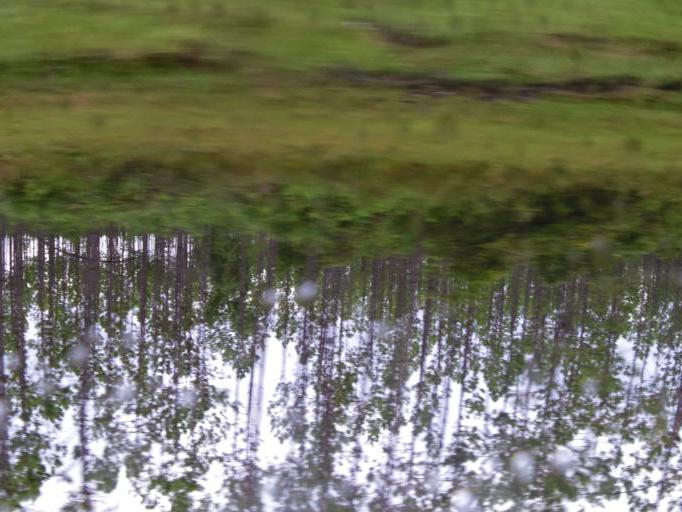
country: US
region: Florida
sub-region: Duval County
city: Baldwin
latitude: 30.4699
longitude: -81.9978
